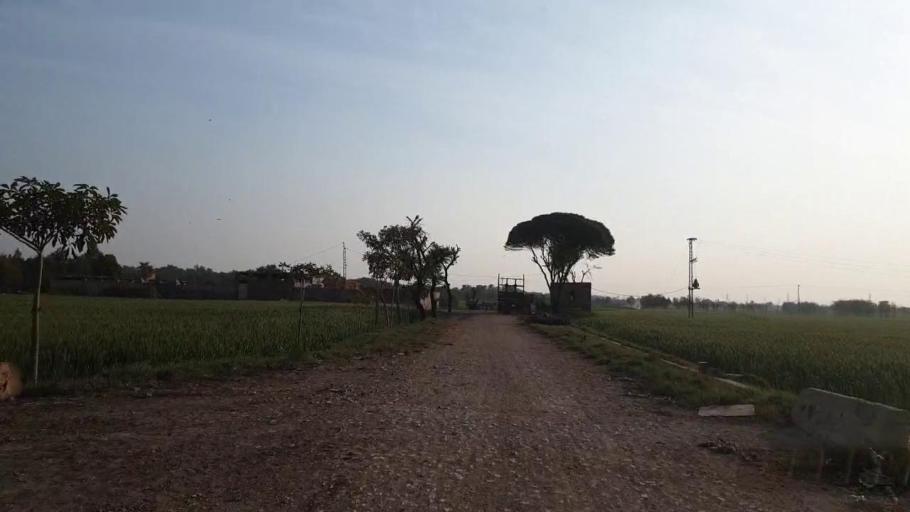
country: PK
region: Sindh
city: Matiari
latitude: 25.5890
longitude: 68.4697
